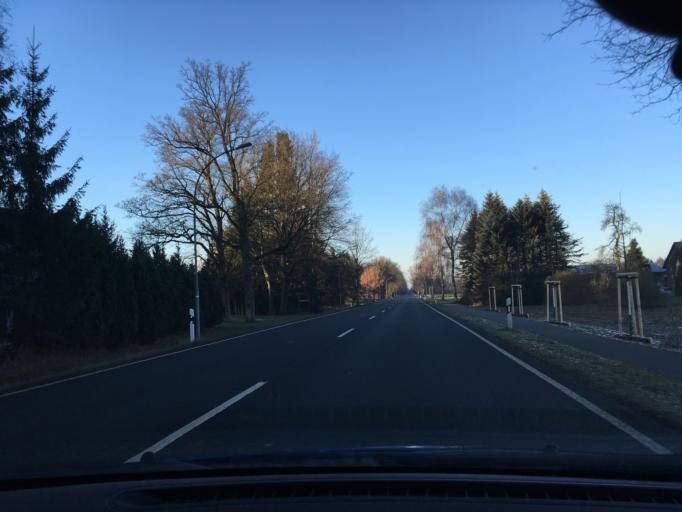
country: DE
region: Lower Saxony
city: Handeloh
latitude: 53.1883
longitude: 9.8335
